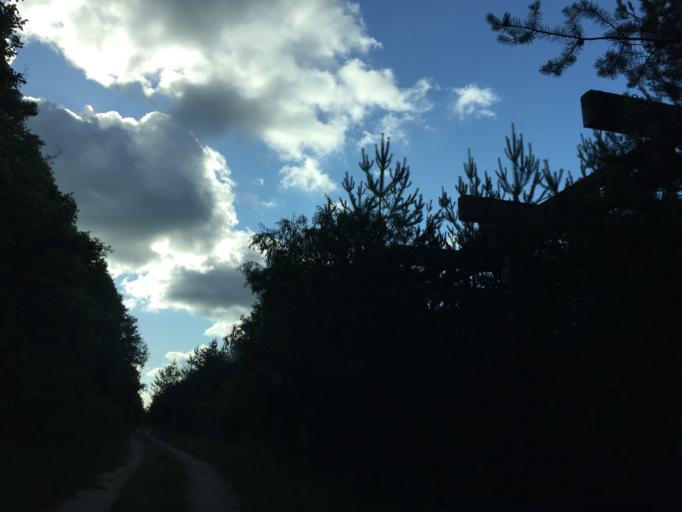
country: LV
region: Ventspils
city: Ventspils
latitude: 57.4099
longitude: 21.6254
